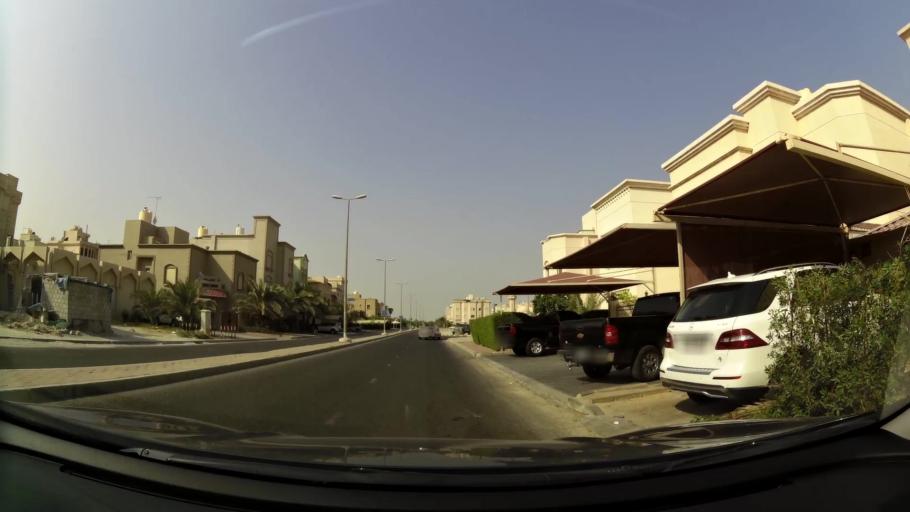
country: KW
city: Bayan
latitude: 29.2856
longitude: 48.0481
